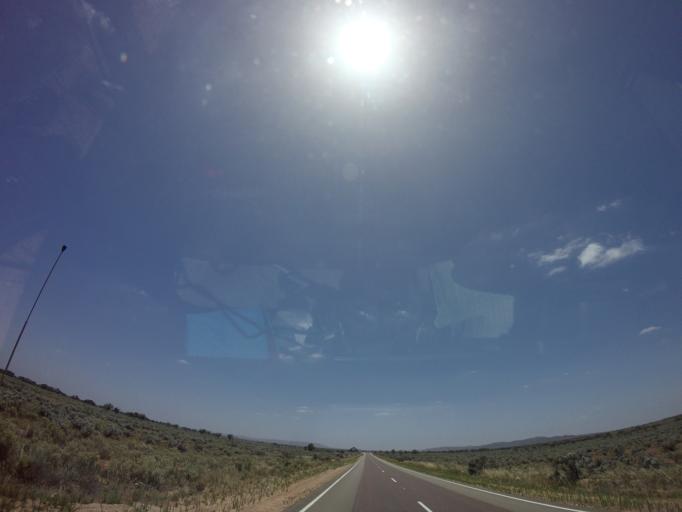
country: AU
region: South Australia
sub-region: Whyalla
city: Whyalla
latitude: -32.8086
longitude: 137.0516
